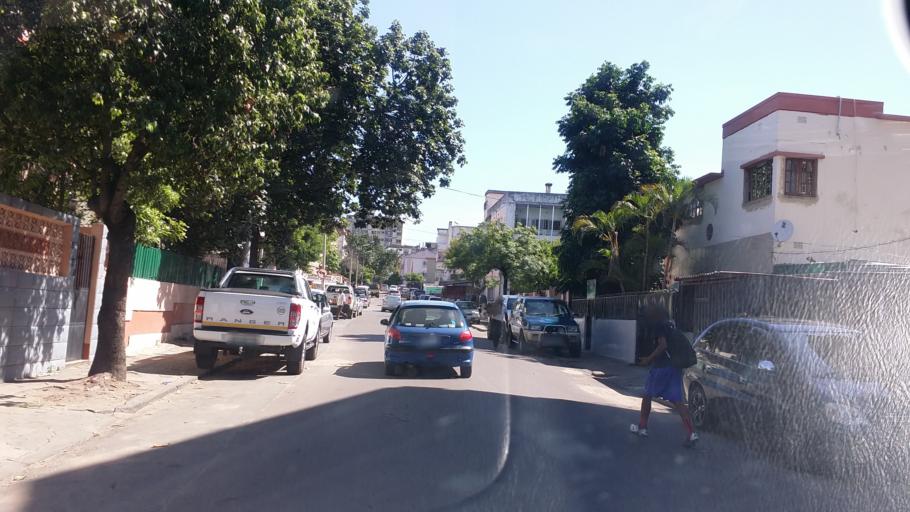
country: MZ
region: Maputo City
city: Maputo
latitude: -25.9583
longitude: 32.5782
